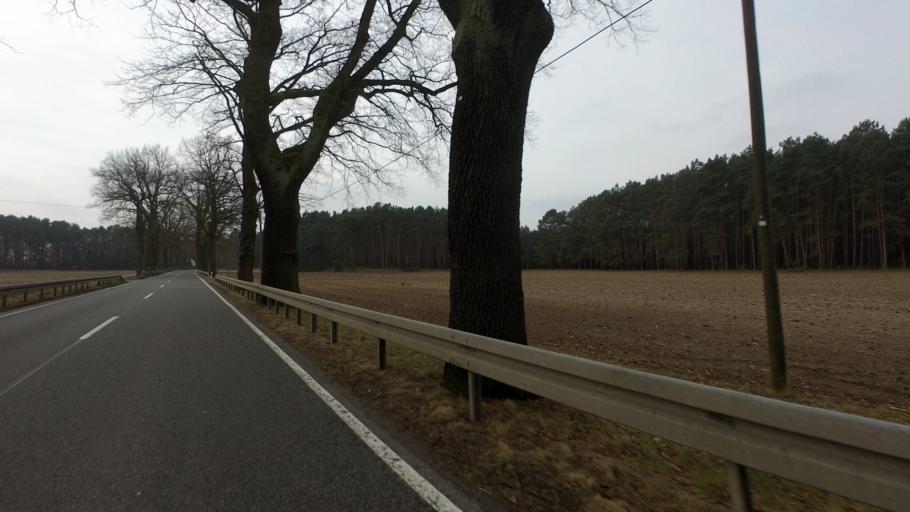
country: DE
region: Brandenburg
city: Beelitz
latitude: 52.2276
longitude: 12.9236
